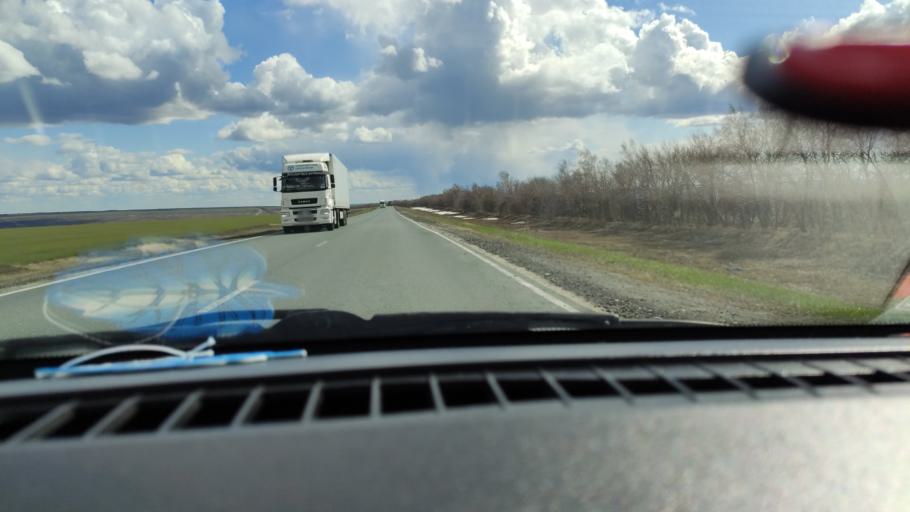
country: RU
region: Saratov
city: Dukhovnitskoye
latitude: 52.7687
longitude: 48.2368
